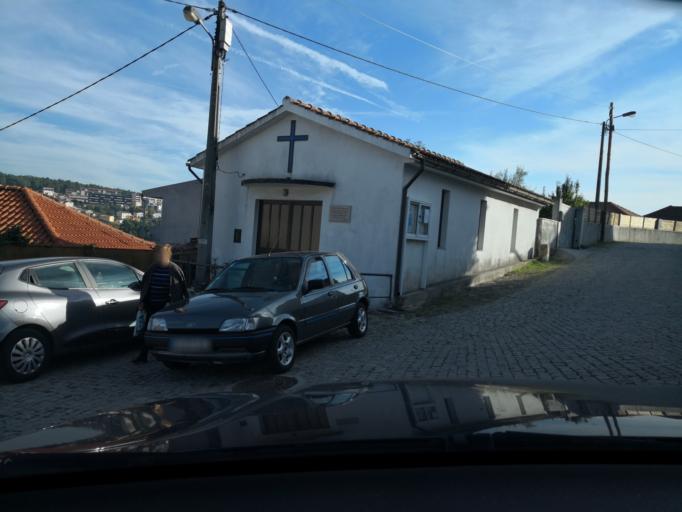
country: PT
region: Vila Real
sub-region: Vila Real
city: Vila Real
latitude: 41.3267
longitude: -7.7398
